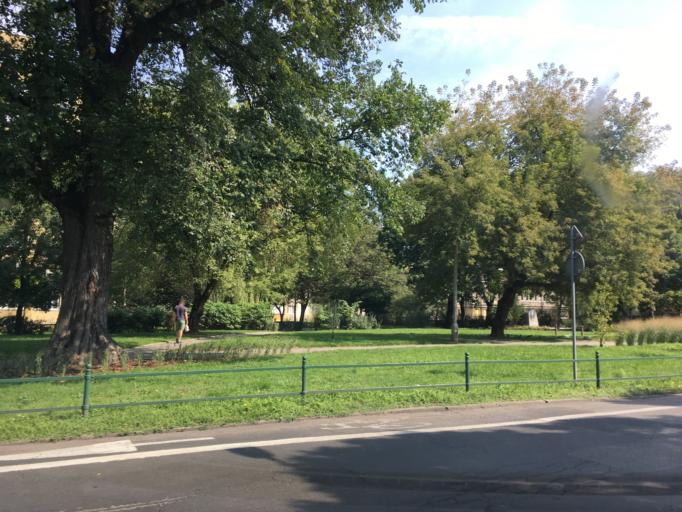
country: PL
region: Lesser Poland Voivodeship
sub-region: Krakow
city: Krakow
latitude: 50.0738
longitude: 19.9257
